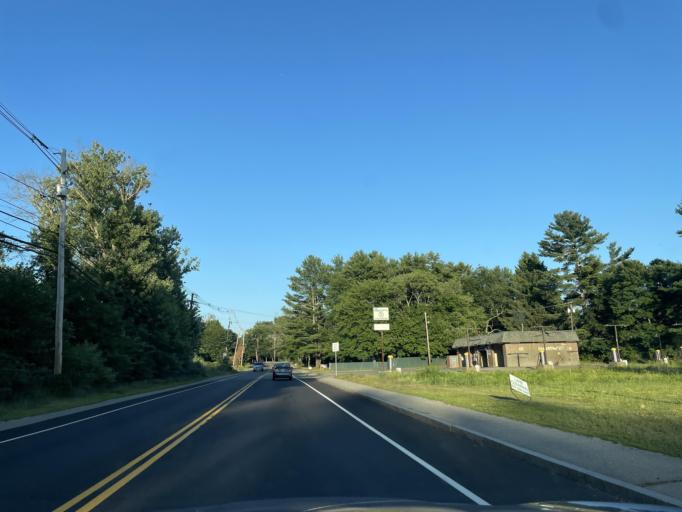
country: US
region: Massachusetts
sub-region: Plymouth County
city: Halifax
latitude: 41.9914
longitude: -70.8534
